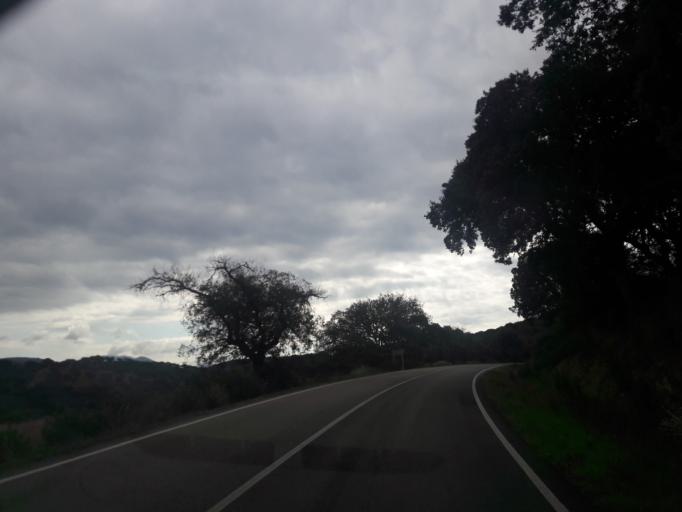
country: ES
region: Castille and Leon
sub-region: Provincia de Salamanca
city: Serradilla del Arroyo
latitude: 40.5202
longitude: -6.4005
